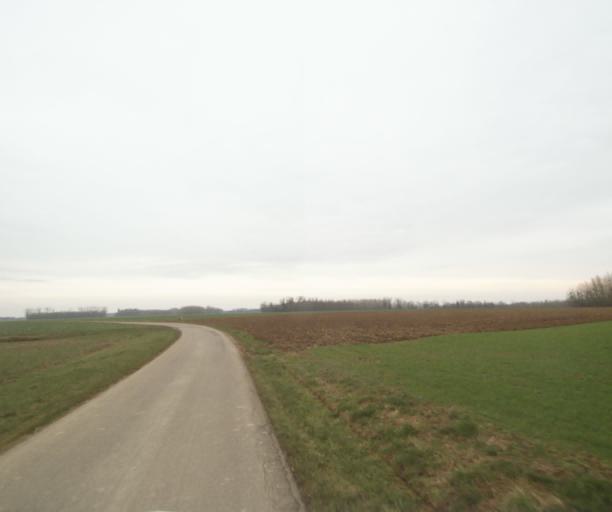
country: FR
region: Champagne-Ardenne
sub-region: Departement de la Haute-Marne
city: Villiers-en-Lieu
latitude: 48.6377
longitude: 4.7781
